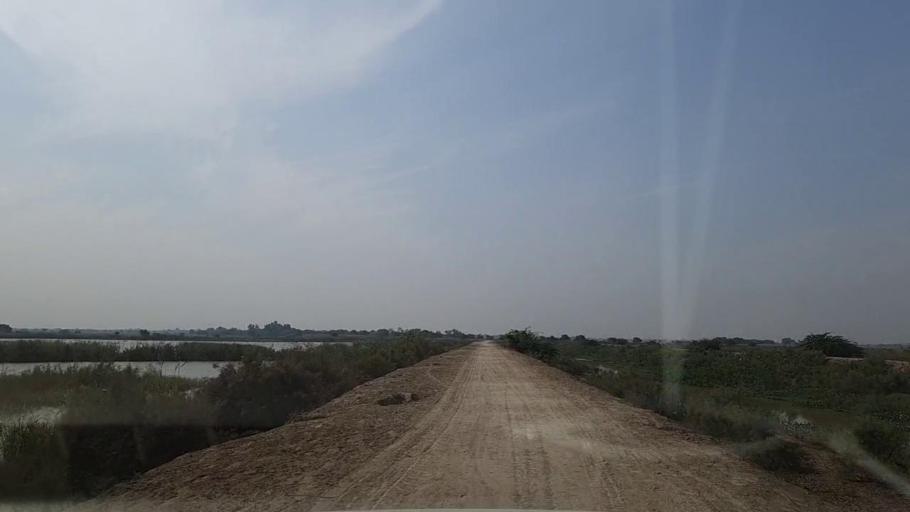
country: PK
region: Sindh
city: Mirpur Batoro
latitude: 24.6579
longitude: 68.2477
